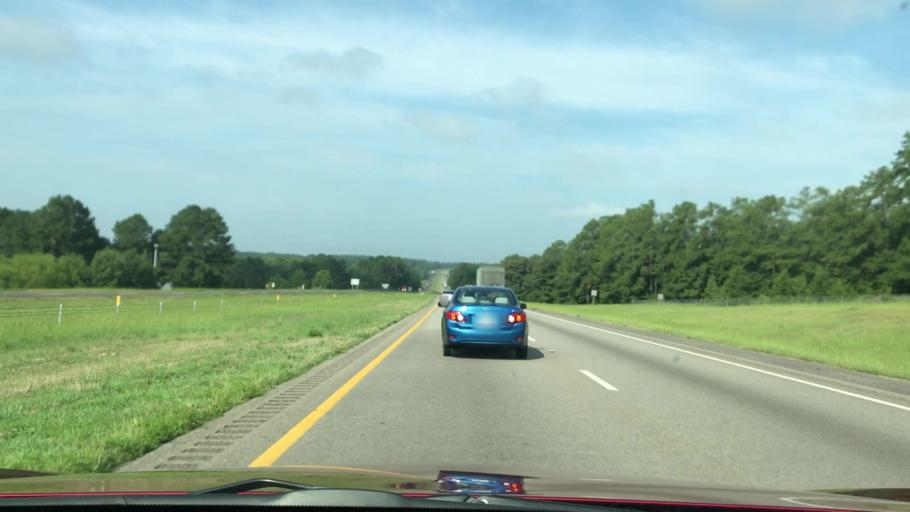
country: US
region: South Carolina
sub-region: Aiken County
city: Aiken
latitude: 33.6526
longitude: -81.7088
